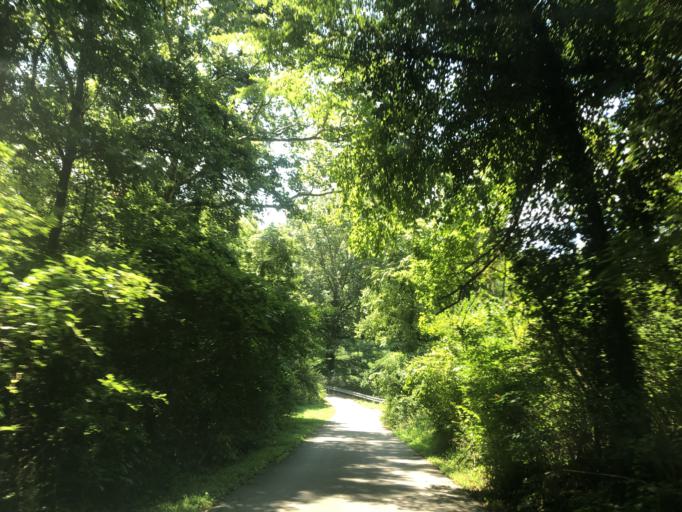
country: US
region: Tennessee
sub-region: Davidson County
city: Lakewood
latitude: 36.1703
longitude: -86.6589
